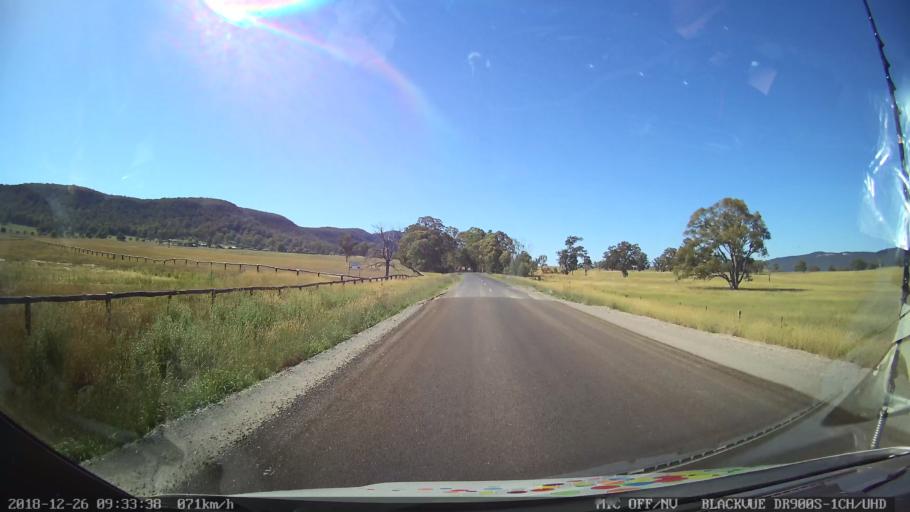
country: AU
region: New South Wales
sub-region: Mid-Western Regional
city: Kandos
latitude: -32.8967
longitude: 150.0355
